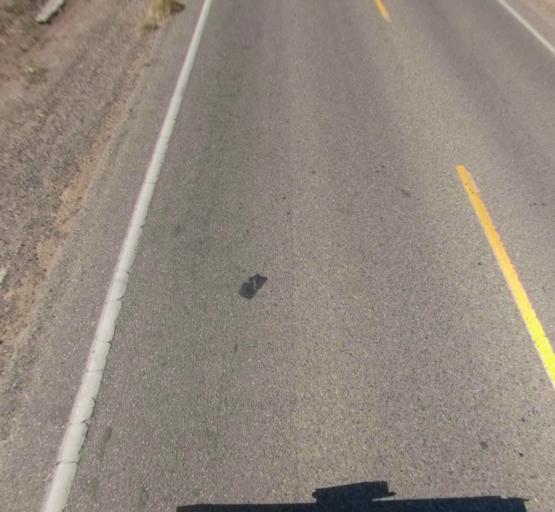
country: US
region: California
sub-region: Madera County
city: Madera Acres
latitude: 37.0059
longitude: -120.1287
